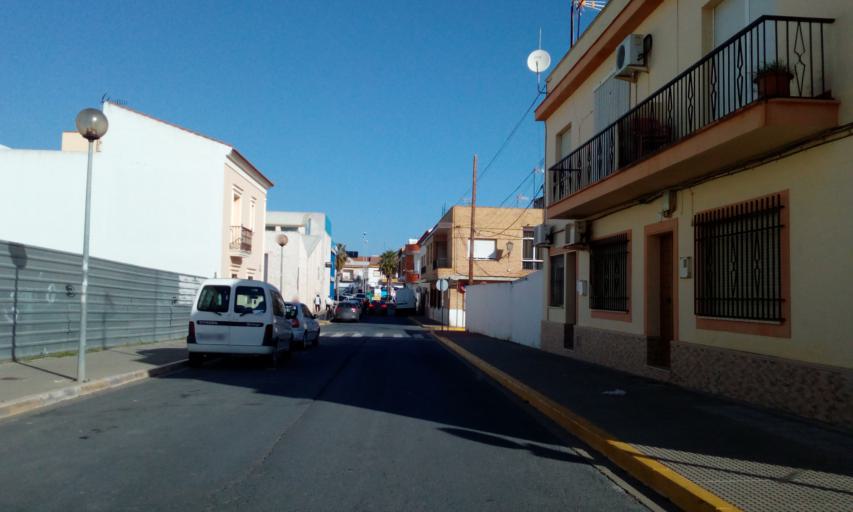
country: ES
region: Andalusia
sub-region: Provincia de Huelva
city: Lepe
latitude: 37.2493
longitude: -7.2036
